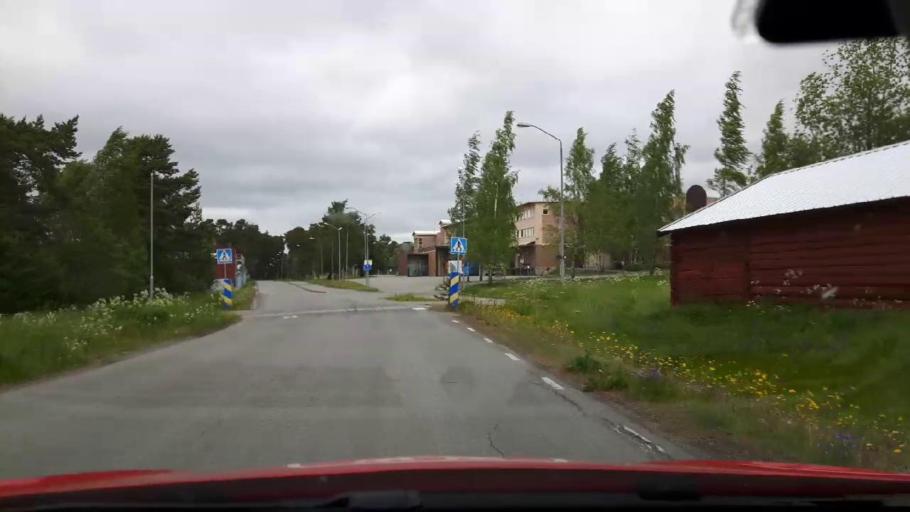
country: SE
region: Jaemtland
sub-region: OEstersunds Kommun
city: Ostersund
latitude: 63.1907
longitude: 14.6316
